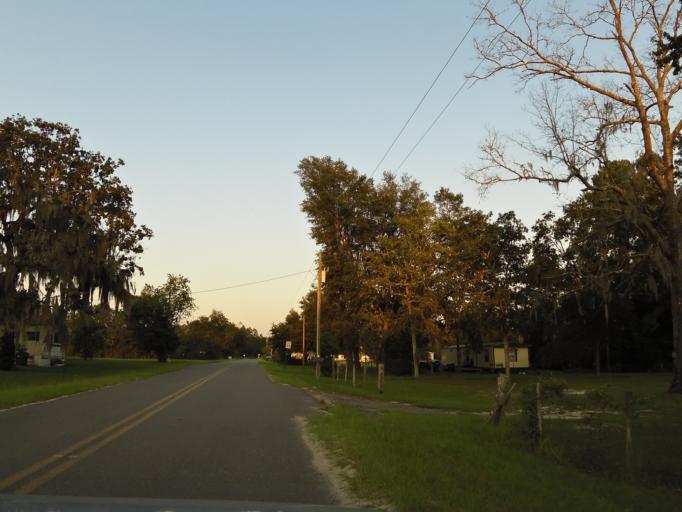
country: US
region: Florida
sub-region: Baker County
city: Macclenny
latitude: 30.3947
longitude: -82.1264
